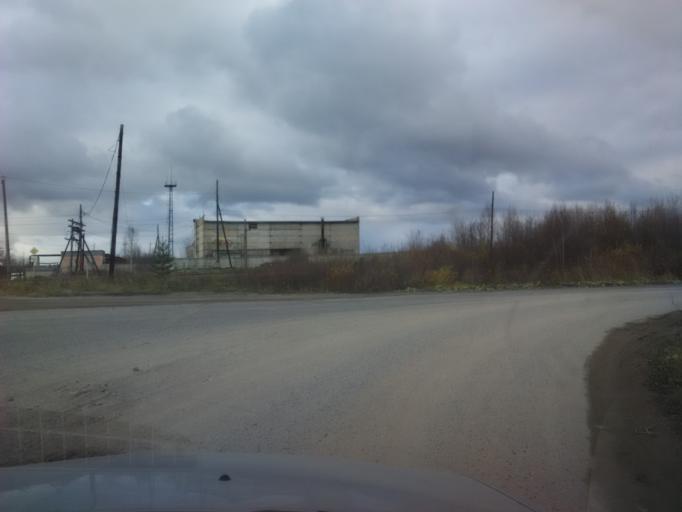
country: RU
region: Murmansk
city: Polyarnyye Zori
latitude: 67.3803
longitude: 32.5096
